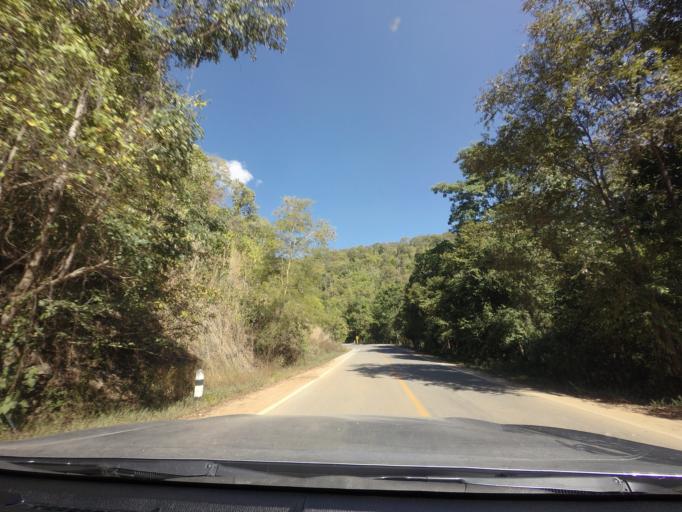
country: TH
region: Lampang
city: Chae Hom
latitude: 18.6357
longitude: 99.6094
